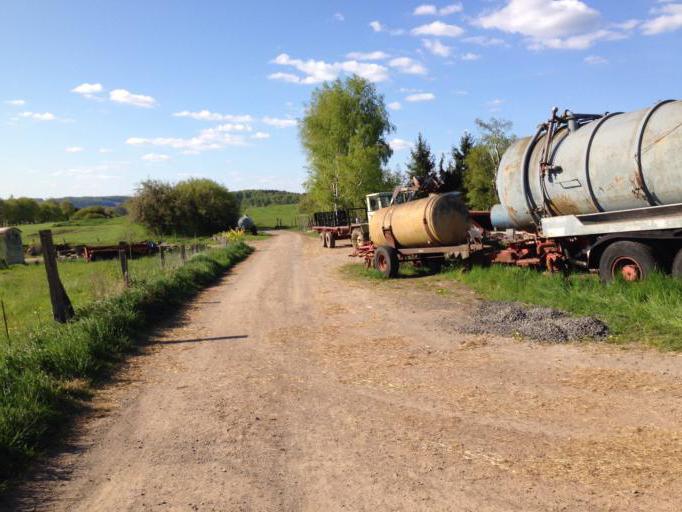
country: DE
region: Hesse
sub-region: Regierungsbezirk Giessen
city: Reiskirchen
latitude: 50.5828
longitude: 8.8174
